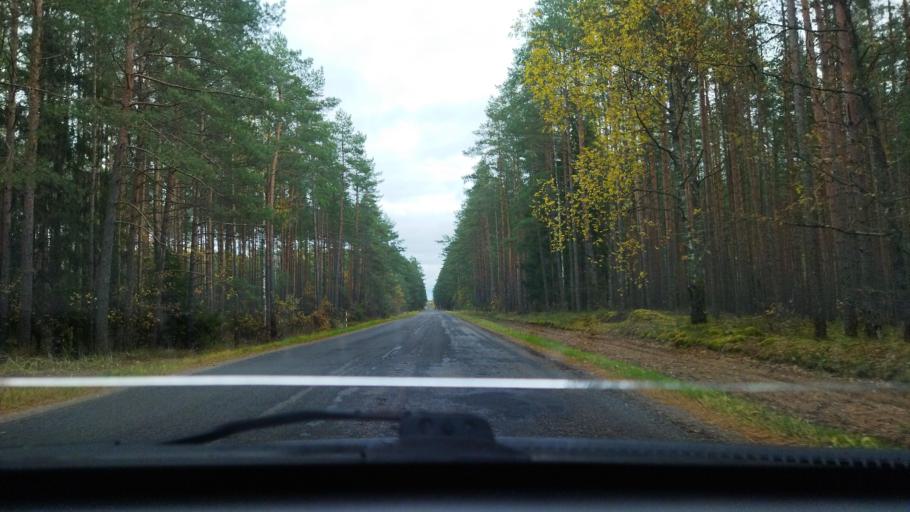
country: BY
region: Minsk
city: Svir
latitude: 54.8102
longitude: 26.2158
